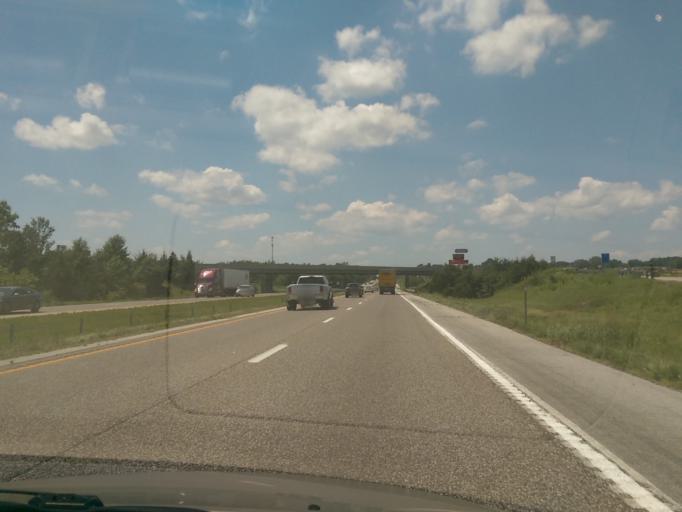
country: US
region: Missouri
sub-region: Boone County
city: Columbia
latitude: 38.9718
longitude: -92.4289
